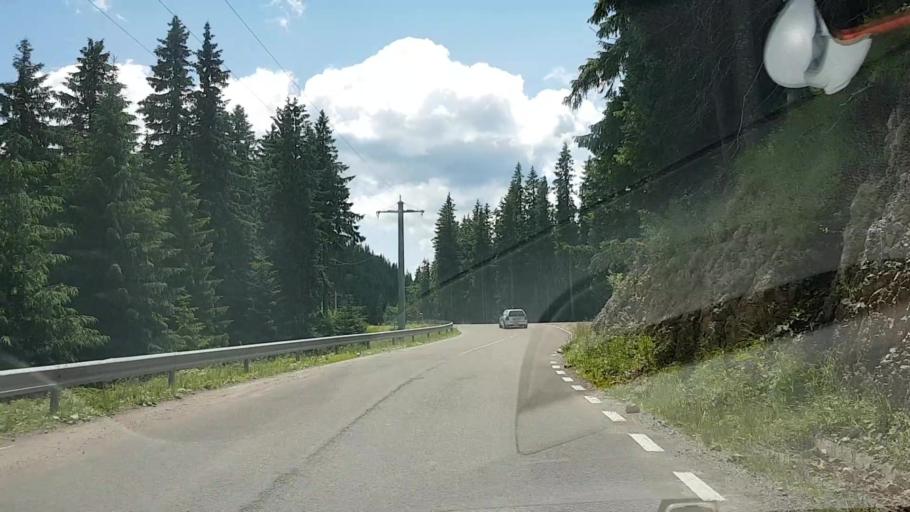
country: RO
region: Suceava
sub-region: Municipiul Campulung Moldovenesc
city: Campulung Moldovenesc
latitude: 47.4536
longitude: 25.5492
